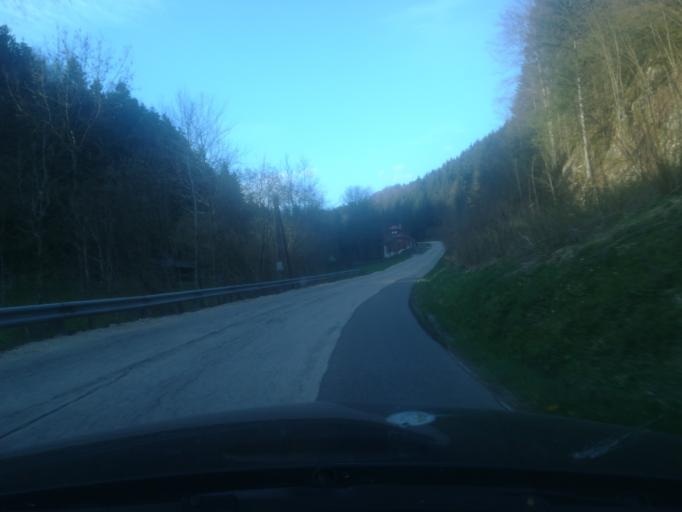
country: AT
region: Upper Austria
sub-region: Politischer Bezirk Perg
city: Bad Kreuzen
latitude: 48.2676
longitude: 14.7875
